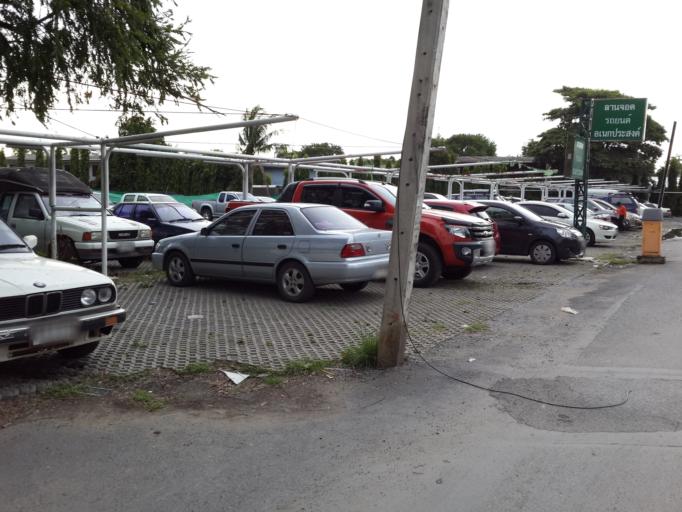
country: TH
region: Bangkok
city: Lak Si
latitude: 13.8766
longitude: 100.5888
